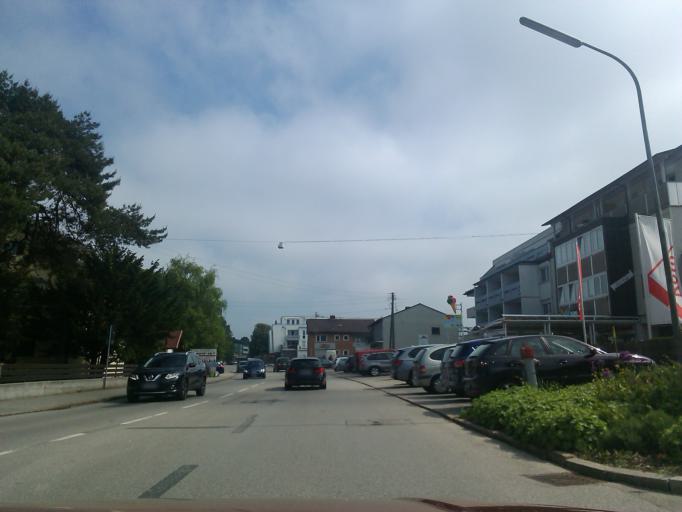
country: DE
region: Bavaria
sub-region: Upper Bavaria
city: Olching
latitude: 48.2034
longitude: 11.3244
